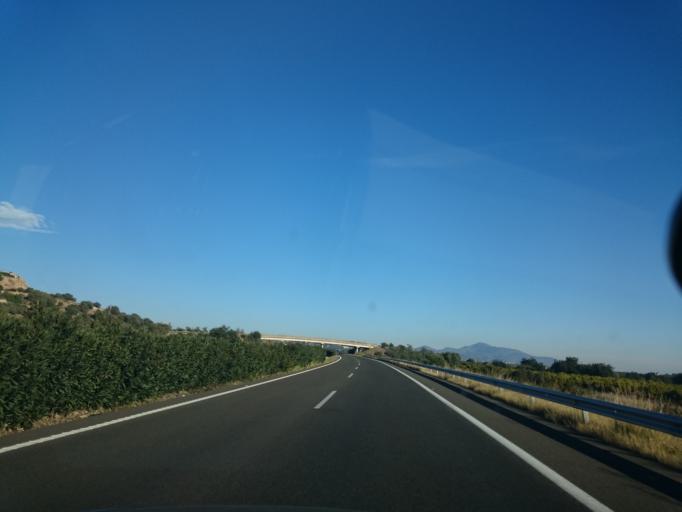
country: ES
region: Valencia
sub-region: Provincia de Castello
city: Benicarlo
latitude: 40.4715
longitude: 0.4179
